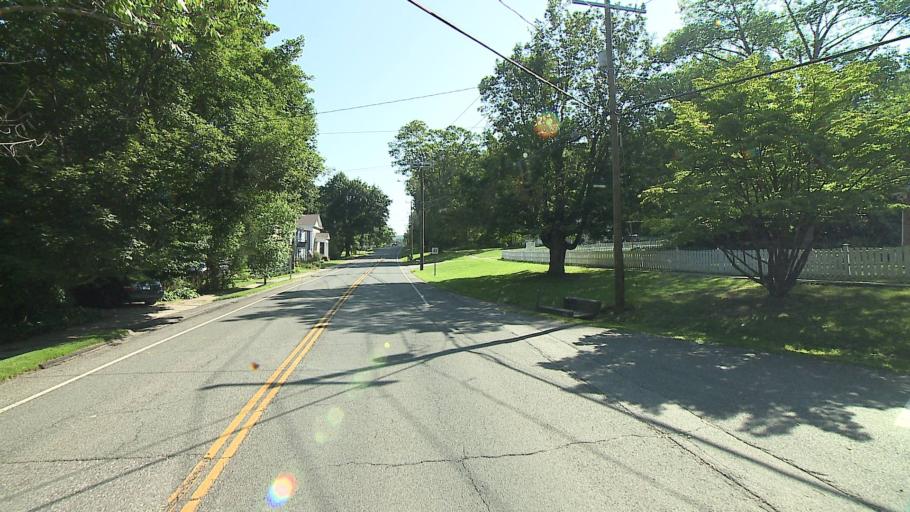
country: US
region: Connecticut
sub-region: Litchfield County
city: Kent
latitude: 41.8816
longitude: -73.4760
